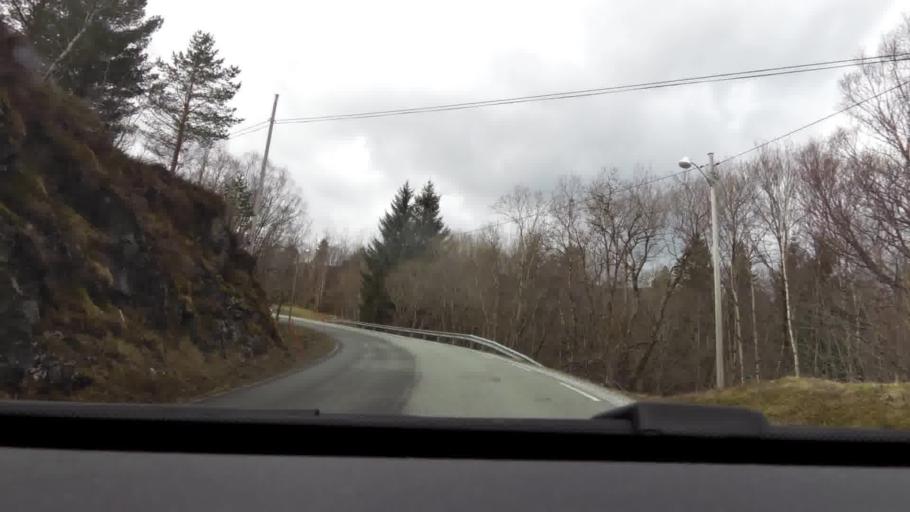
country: NO
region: More og Romsdal
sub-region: Eide
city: Eide
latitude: 62.9088
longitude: 7.5313
